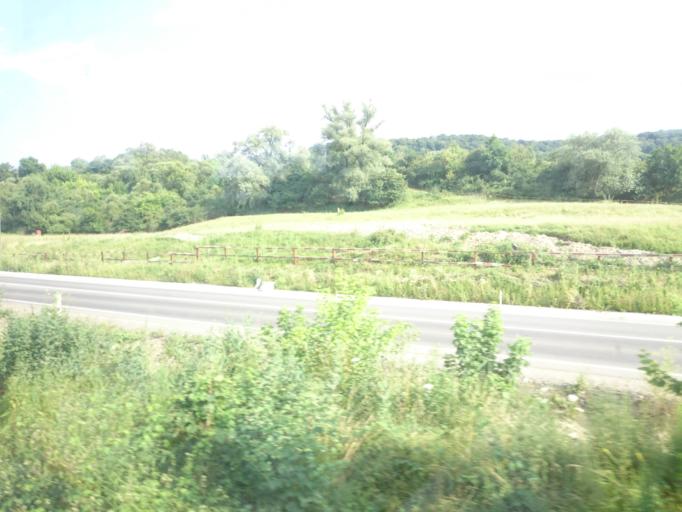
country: RO
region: Sibiu
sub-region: Oras Dumbraveni
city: Dumbraveni
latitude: 46.2164
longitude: 24.5700
